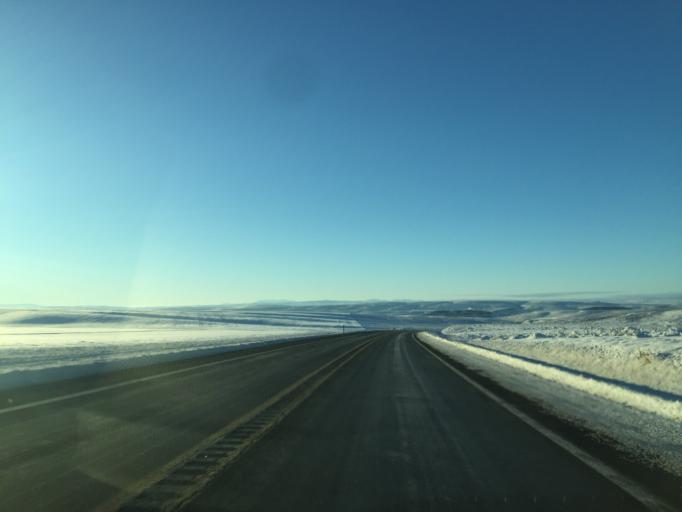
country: US
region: Washington
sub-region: Grant County
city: Soap Lake
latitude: 47.5994
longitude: -119.6064
